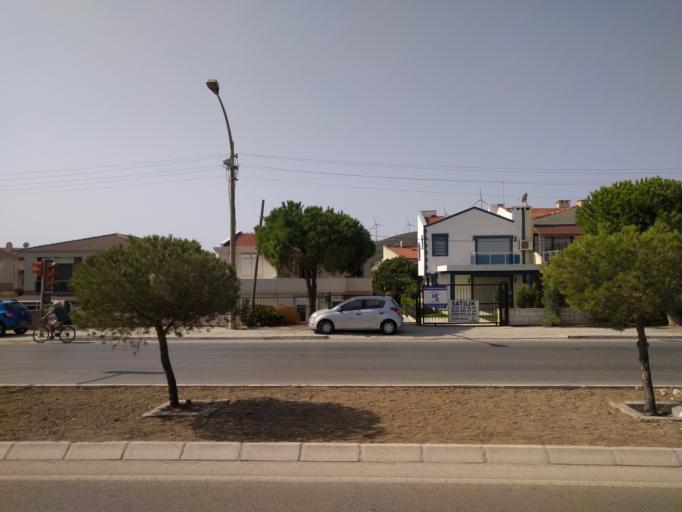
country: TR
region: Izmir
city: Alacati
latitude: 38.3045
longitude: 26.3606
